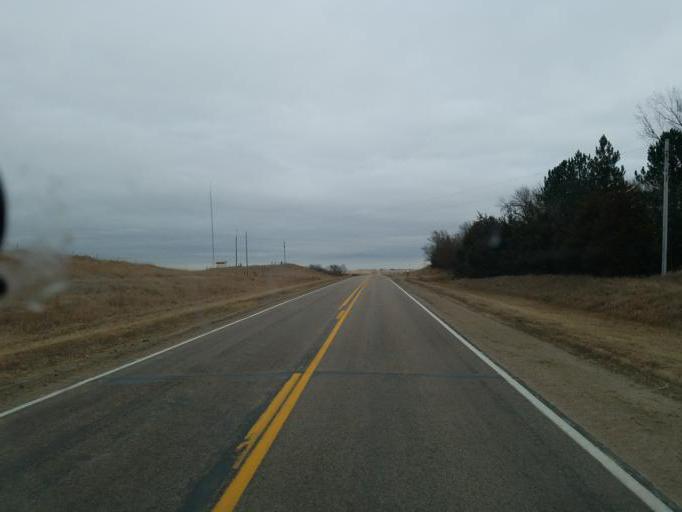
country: US
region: Nebraska
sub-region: Knox County
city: Bloomfield
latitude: 42.5979
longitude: -97.5704
